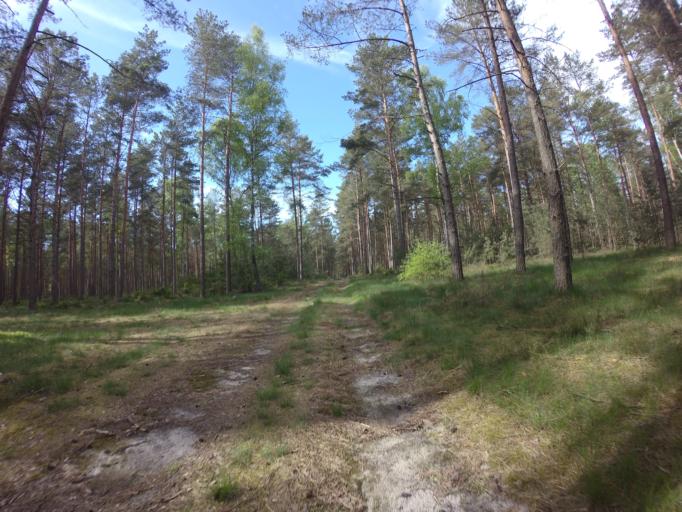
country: PL
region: West Pomeranian Voivodeship
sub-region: Powiat choszczenski
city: Drawno
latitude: 53.1925
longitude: 15.7344
